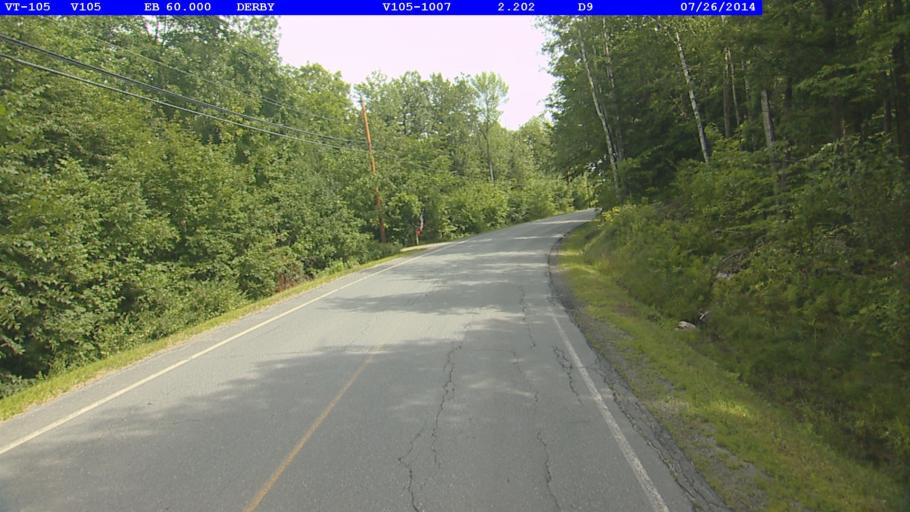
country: US
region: Vermont
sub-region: Orleans County
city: Newport
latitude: 44.9296
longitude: -72.1131
